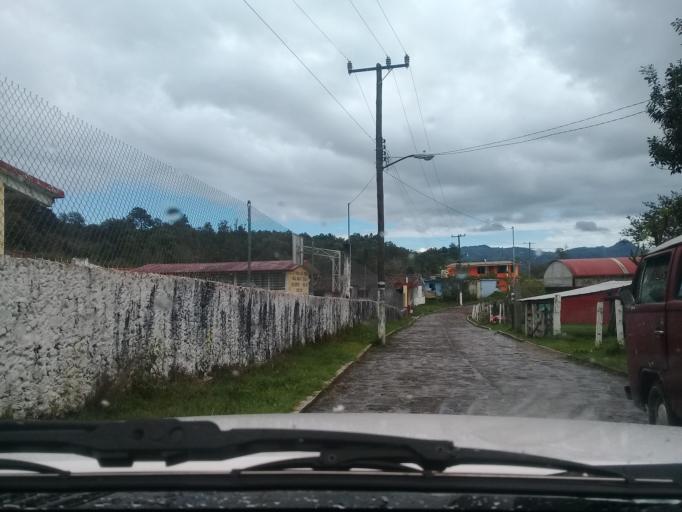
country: MX
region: Veracruz
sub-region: Acajete
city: La Joya
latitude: 19.6187
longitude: -97.0018
